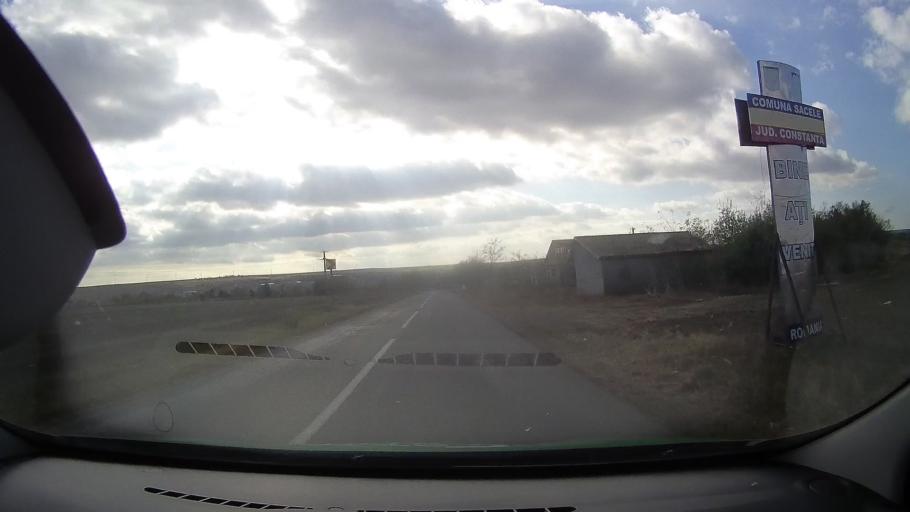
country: RO
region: Constanta
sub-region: Comuna Sacele
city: Sacele
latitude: 44.4910
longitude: 28.6534
